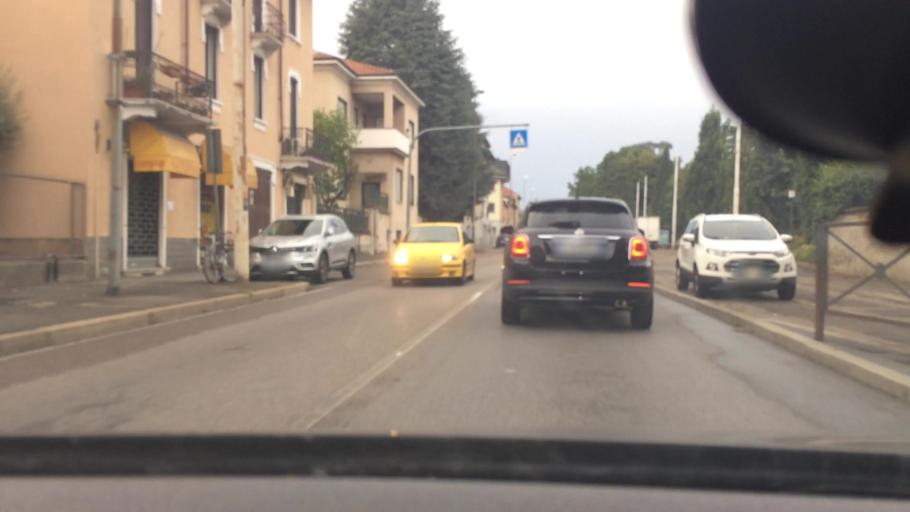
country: IT
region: Lombardy
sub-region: Provincia di Monza e Brianza
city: Nova Milanese
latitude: 45.5894
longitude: 9.1970
